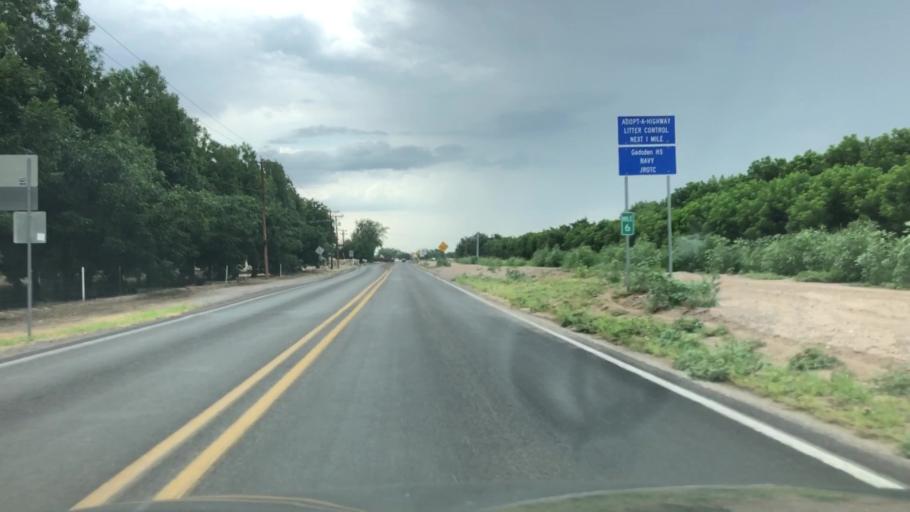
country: US
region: New Mexico
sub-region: Dona Ana County
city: La Union
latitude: 31.9945
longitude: -106.6534
